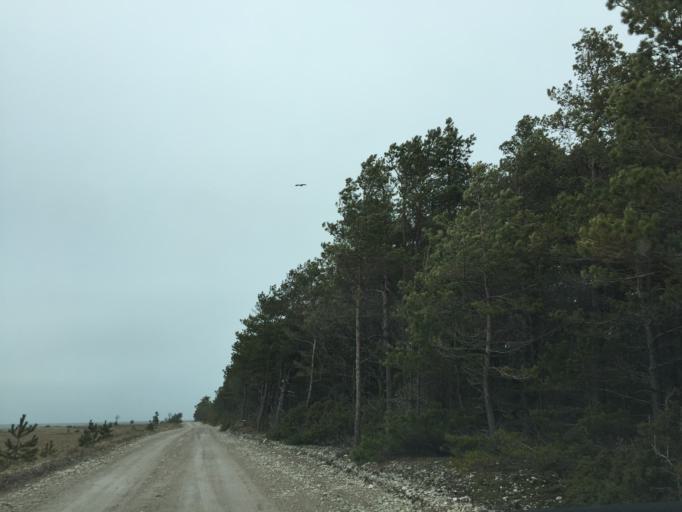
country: EE
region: Saare
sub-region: Kuressaare linn
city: Kuressaare
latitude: 58.5012
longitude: 21.9151
